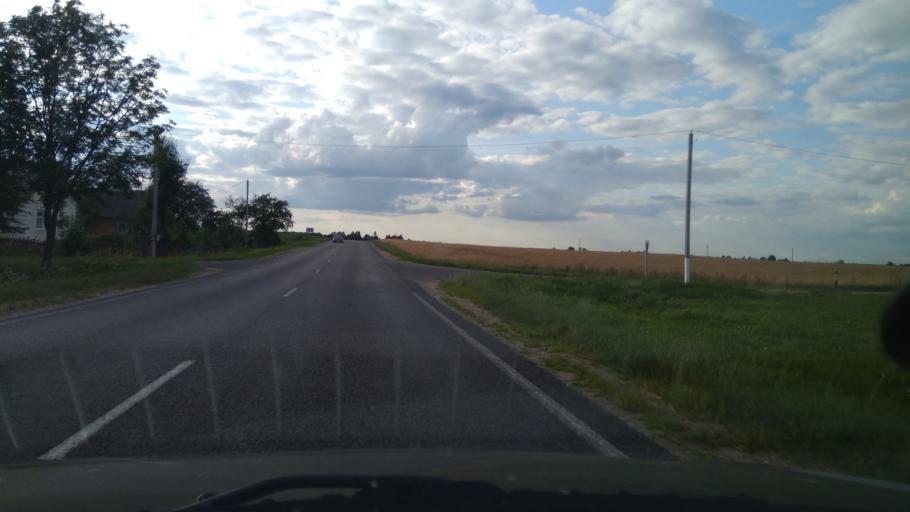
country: BY
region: Grodnenskaya
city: Masty
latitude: 53.3129
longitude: 24.6947
